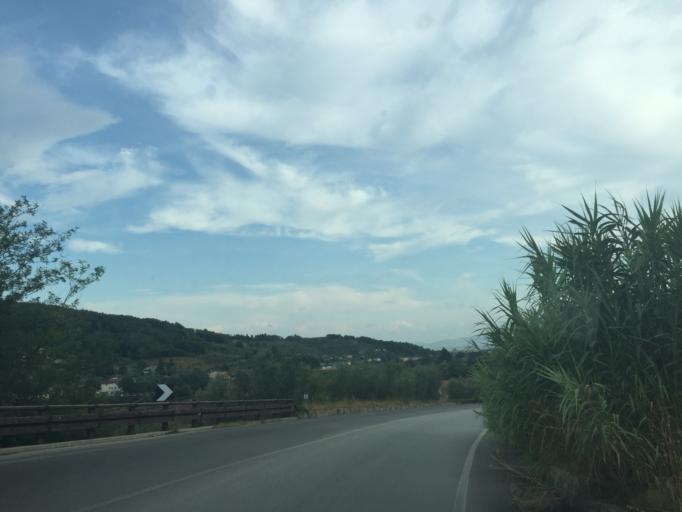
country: IT
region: Tuscany
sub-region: Provincia di Pistoia
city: Pistoia
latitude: 43.9738
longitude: 10.8882
